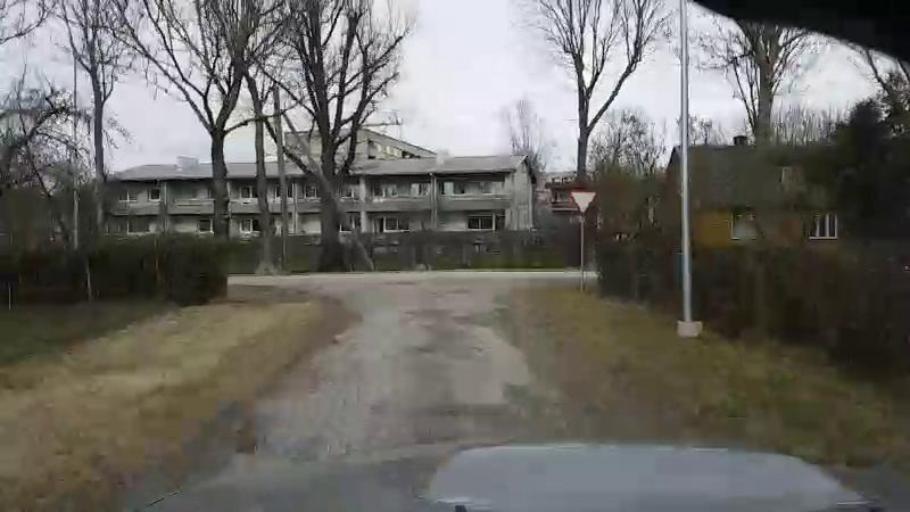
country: EE
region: Jaervamaa
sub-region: Paide linn
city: Paide
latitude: 58.8814
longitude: 25.5690
